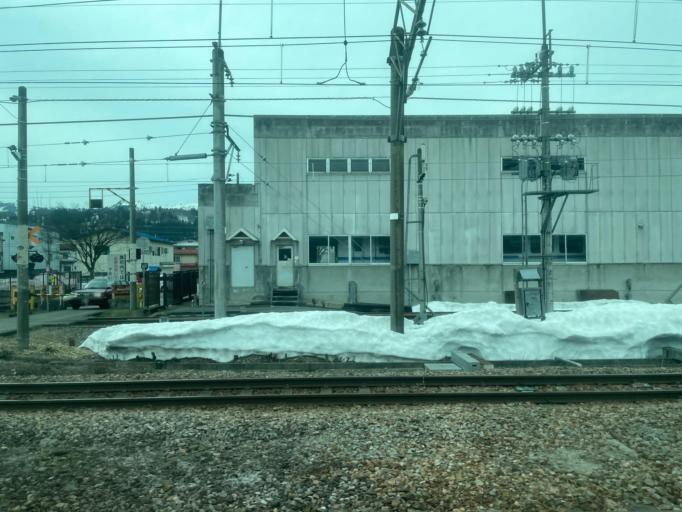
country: JP
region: Niigata
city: Muikamachi
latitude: 37.0649
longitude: 138.8744
